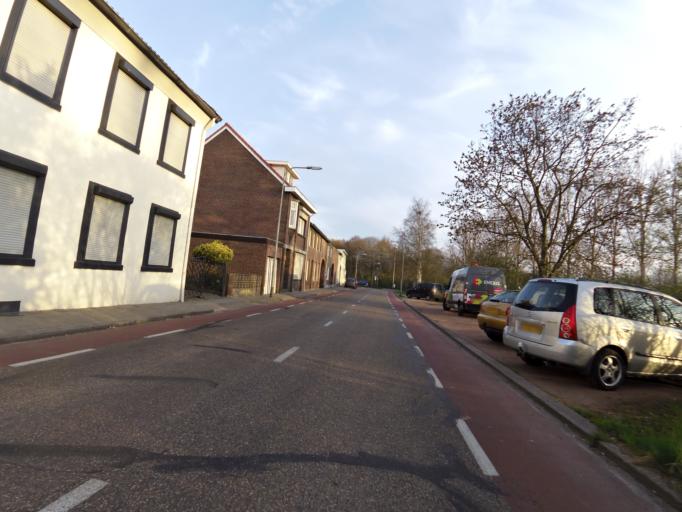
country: NL
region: Limburg
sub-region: Gemeente Kerkrade
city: Kerkrade
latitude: 50.9060
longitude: 6.0429
